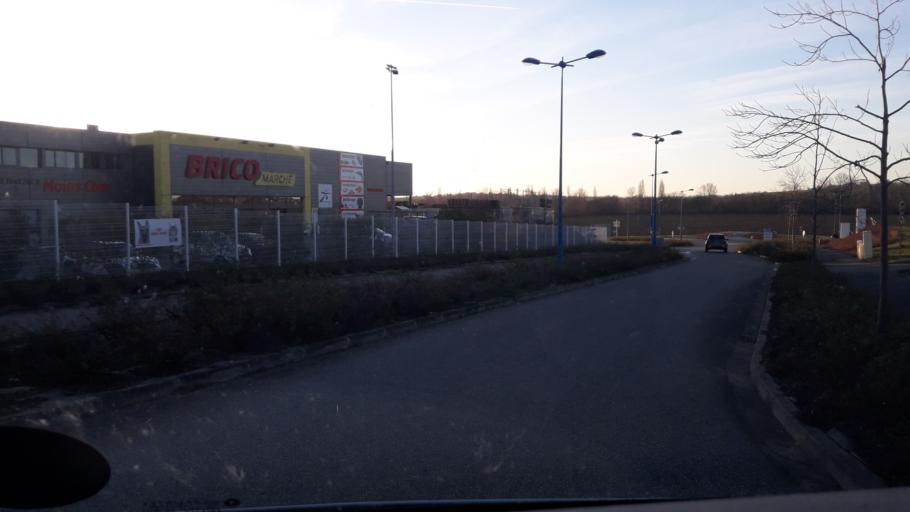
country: FR
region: Midi-Pyrenees
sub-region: Departement du Gers
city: Pujaudran
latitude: 43.6007
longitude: 1.0690
